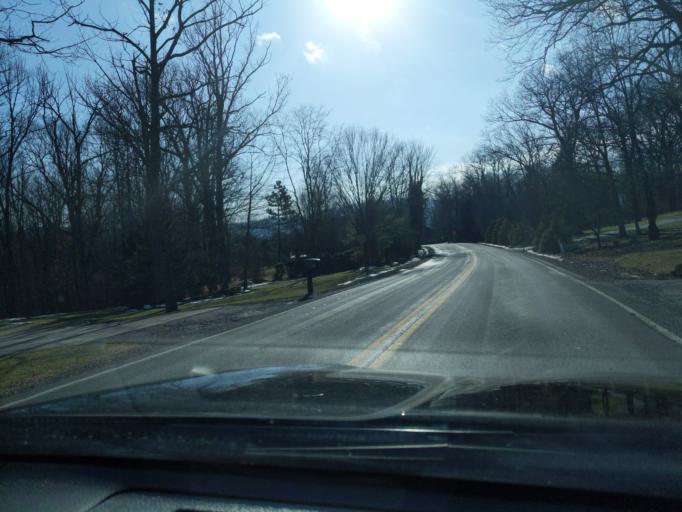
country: US
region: Pennsylvania
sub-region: Blair County
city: Lakemont
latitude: 40.4655
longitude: -78.3744
